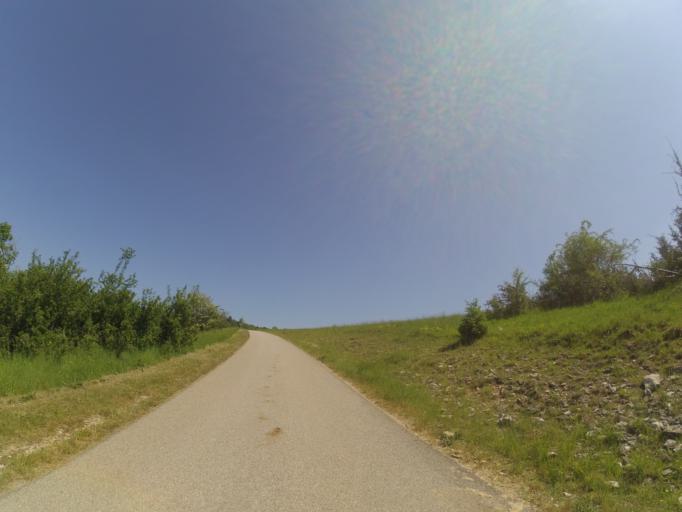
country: DE
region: Baden-Wuerttemberg
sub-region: Tuebingen Region
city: Merklingen
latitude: 48.5075
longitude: 9.7644
